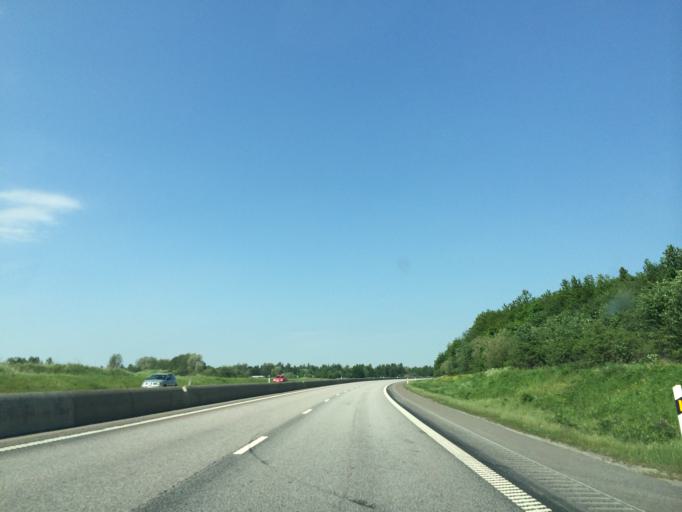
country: SE
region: OEstergoetland
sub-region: Norrkopings Kommun
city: Norrkoping
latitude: 58.5990
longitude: 16.1266
